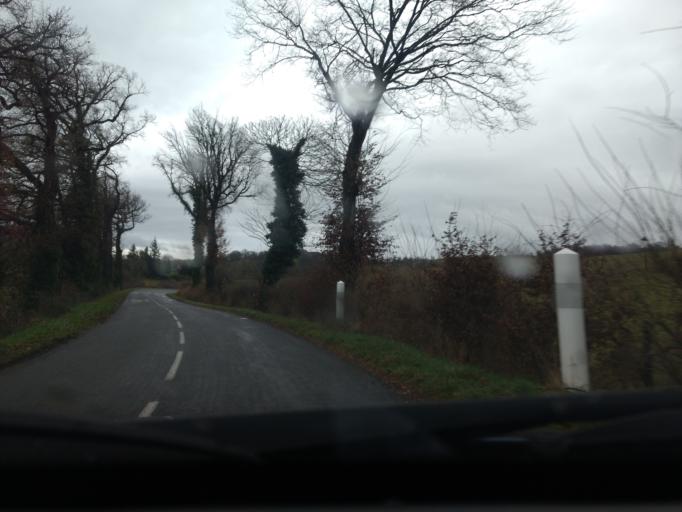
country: FR
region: Midi-Pyrenees
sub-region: Departement de l'Aveyron
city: Livinhac-le-Haut
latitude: 44.6096
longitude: 2.1780
